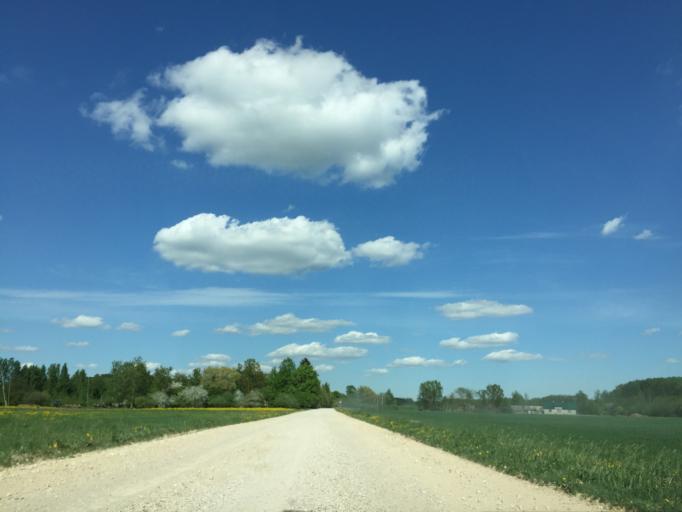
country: LV
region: Rundales
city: Pilsrundale
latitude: 56.3660
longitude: 24.0407
